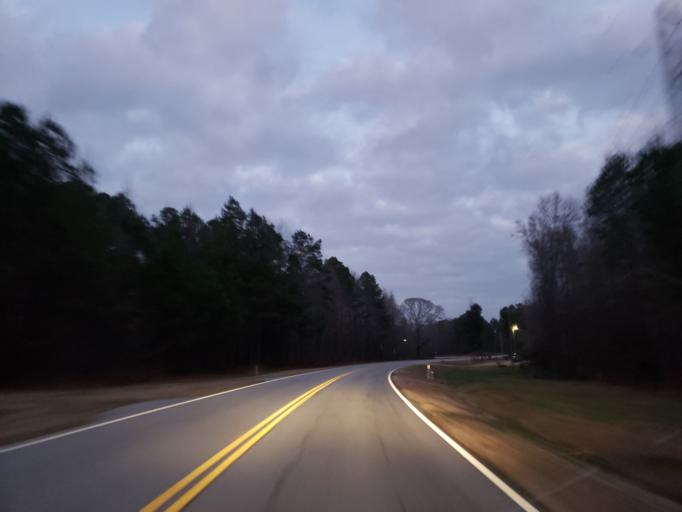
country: US
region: Georgia
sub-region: Carroll County
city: Temple
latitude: 33.7965
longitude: -85.0606
